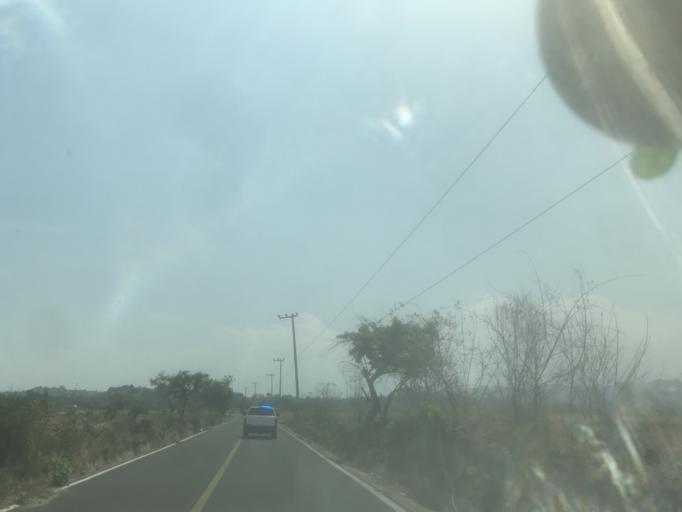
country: MX
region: Morelos
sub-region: Yecapixtla
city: Achichipico
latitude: 18.9571
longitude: -98.8303
